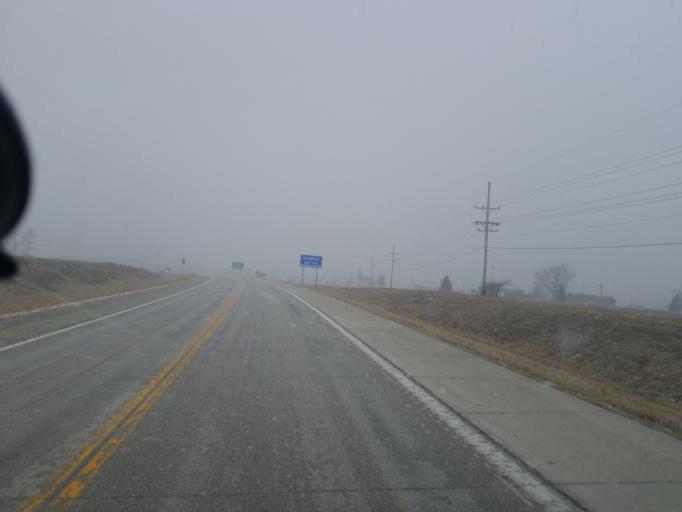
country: US
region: Missouri
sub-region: Adair County
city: Kirksville
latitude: 40.2447
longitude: -92.5826
